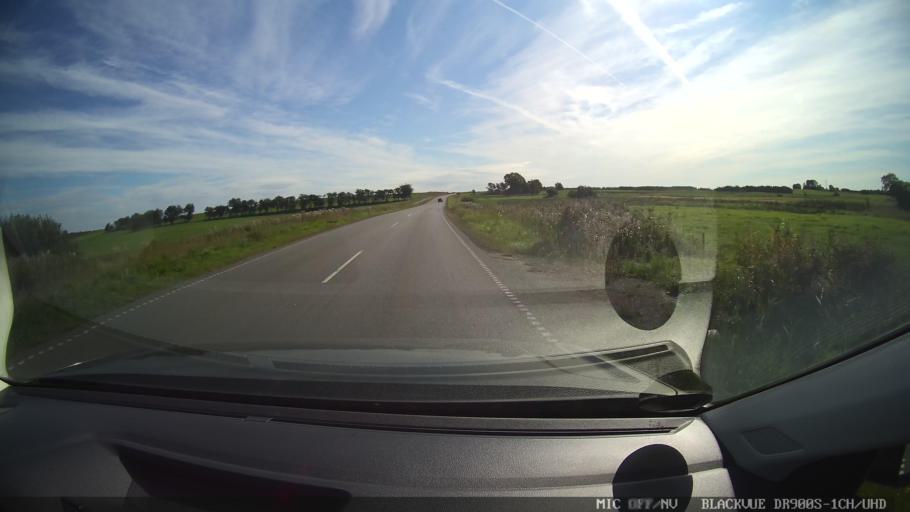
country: DK
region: North Denmark
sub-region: Mariagerfjord Kommune
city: Arden
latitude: 56.7652
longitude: 9.8931
